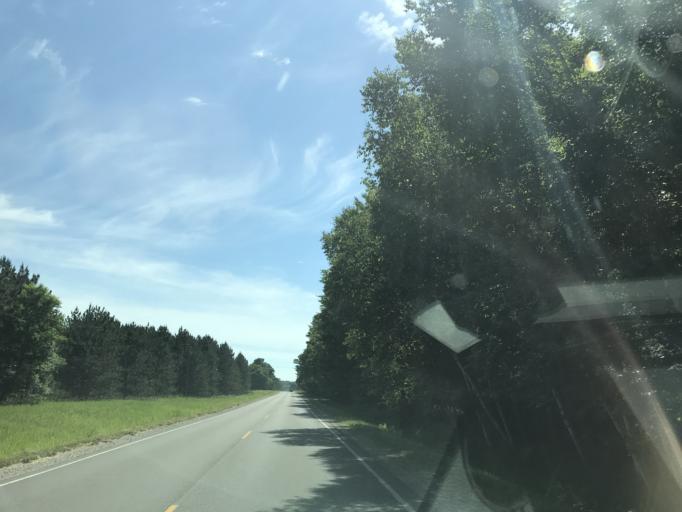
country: US
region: Michigan
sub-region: Grand Traverse County
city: Traverse City
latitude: 44.6543
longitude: -85.7124
